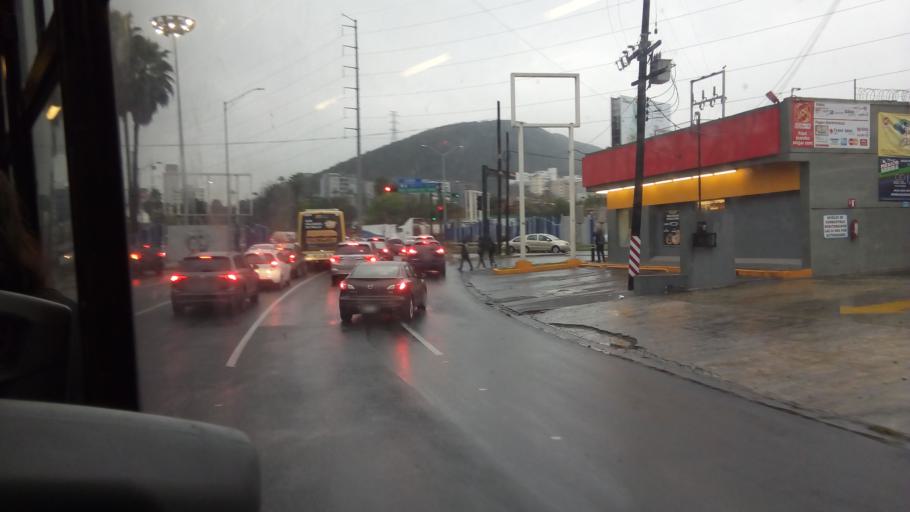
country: MX
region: Nuevo Leon
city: Garza Garcia
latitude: 25.6751
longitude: -100.3638
